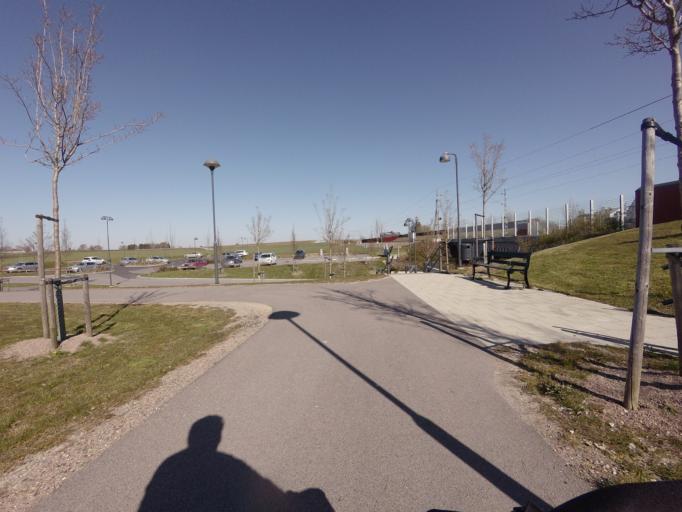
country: SE
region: Skane
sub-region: Malmo
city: Oxie
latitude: 55.4688
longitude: 13.1317
